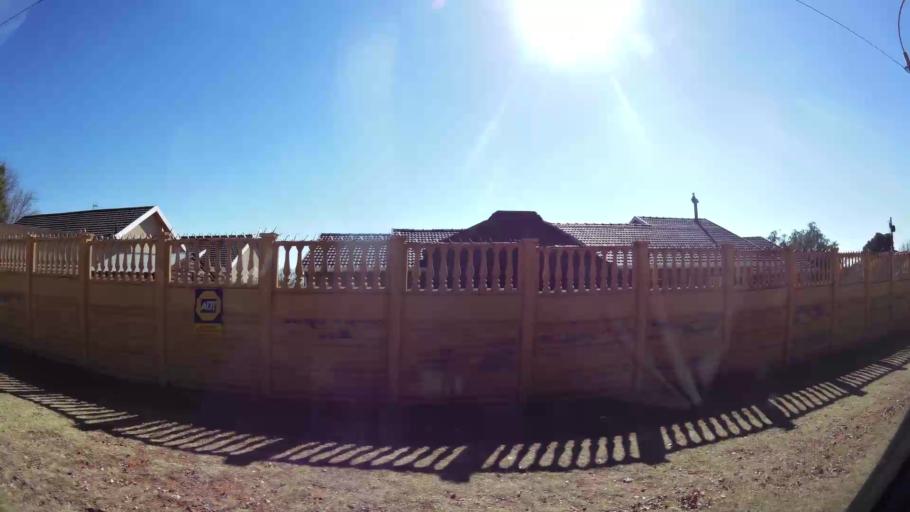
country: ZA
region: Gauteng
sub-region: City of Johannesburg Metropolitan Municipality
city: Roodepoort
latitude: -26.1220
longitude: 27.8481
